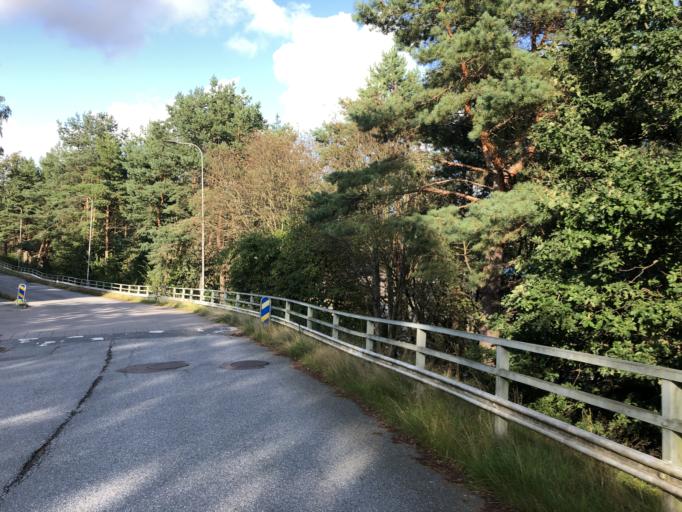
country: SE
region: Vaestra Goetaland
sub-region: Goteborg
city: Majorna
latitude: 57.7316
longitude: 11.8985
